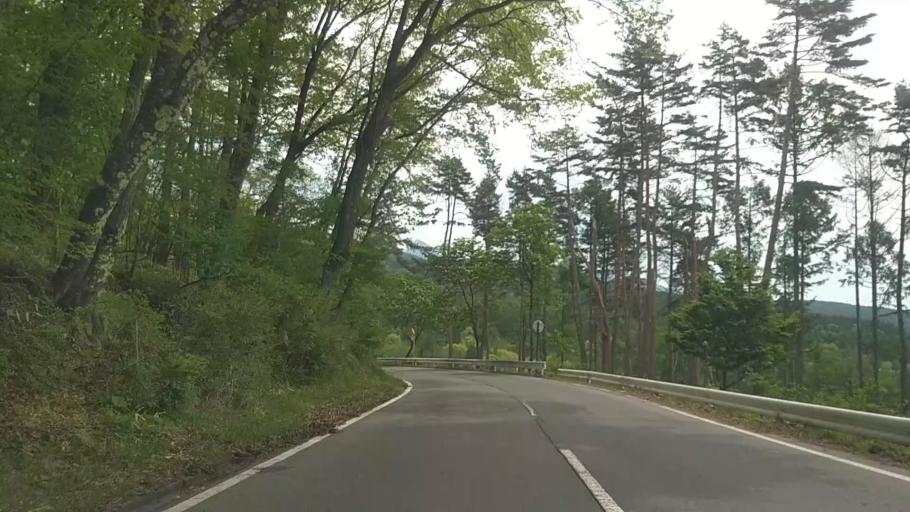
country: JP
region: Nagano
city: Chino
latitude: 36.0424
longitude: 138.2681
